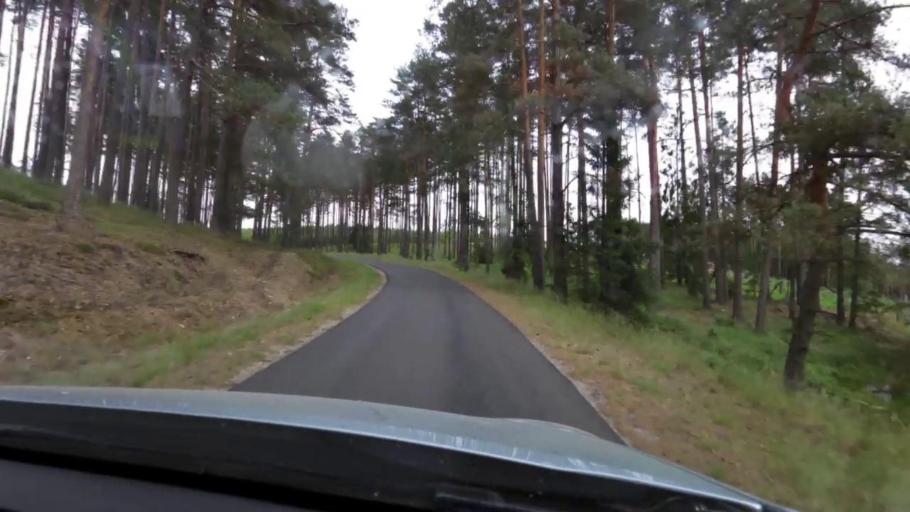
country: PL
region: Pomeranian Voivodeship
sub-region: Powiat bytowski
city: Trzebielino
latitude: 54.1965
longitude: 17.0233
